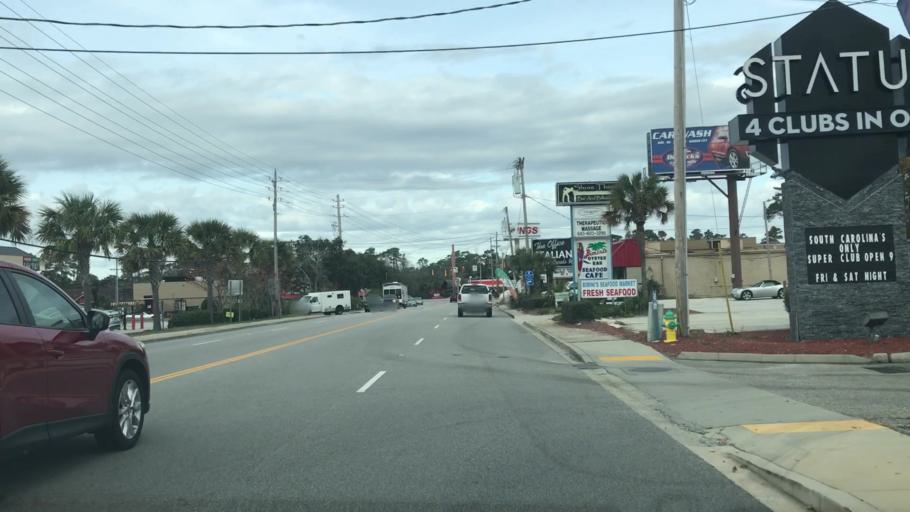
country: US
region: South Carolina
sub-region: Horry County
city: North Myrtle Beach
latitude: 33.7772
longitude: -78.7914
